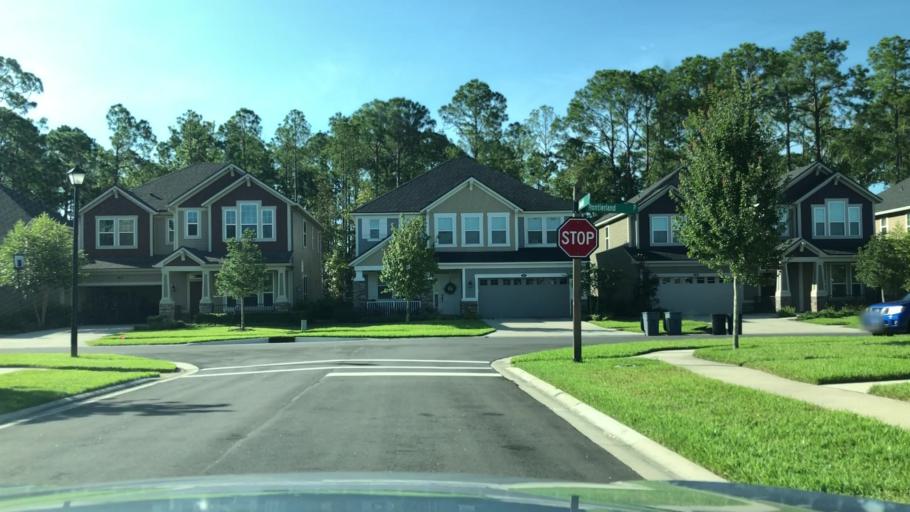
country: US
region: Florida
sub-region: Saint Johns County
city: Palm Valley
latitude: 30.1306
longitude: -81.4210
